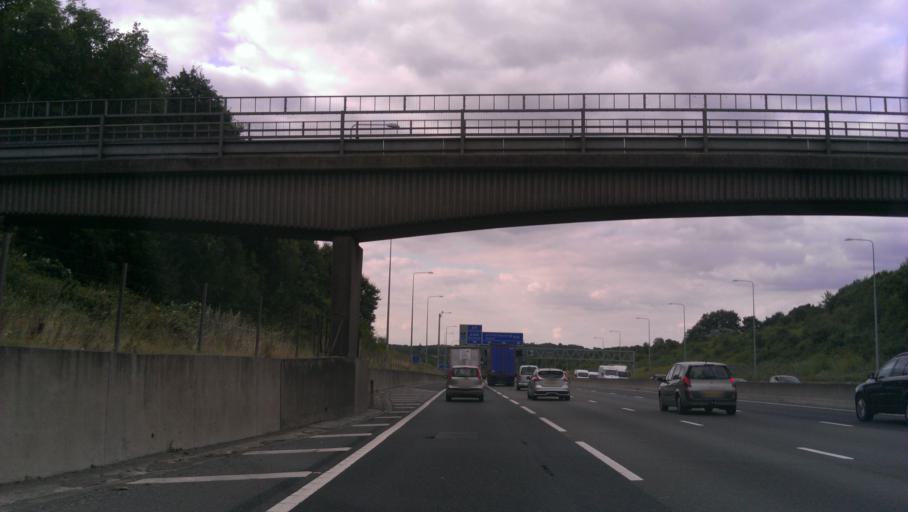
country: GB
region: England
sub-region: Greater London
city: Cranham
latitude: 51.5953
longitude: 0.2688
